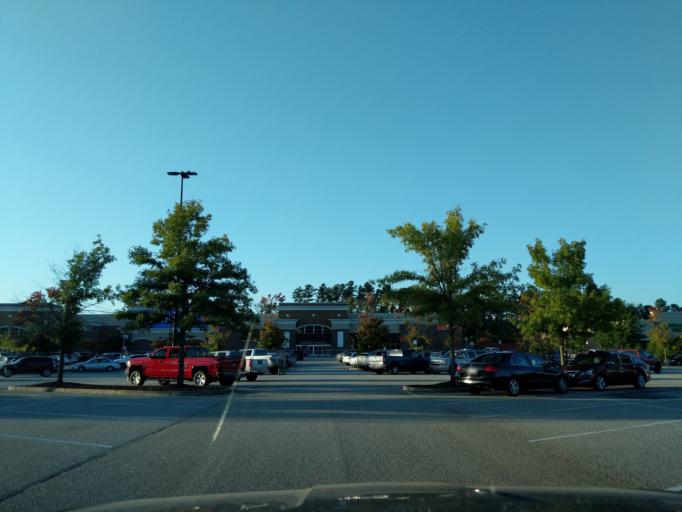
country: US
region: Georgia
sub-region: Columbia County
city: Grovetown
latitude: 33.4804
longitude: -82.1951
